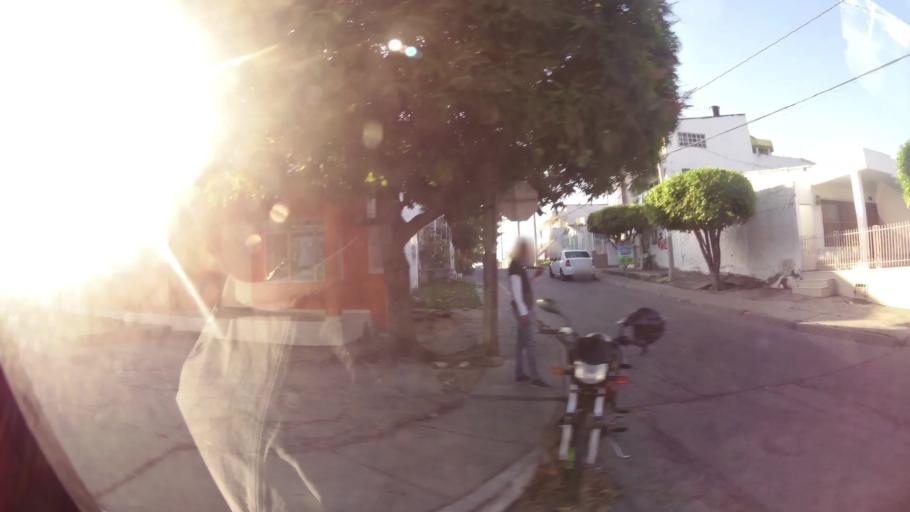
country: CO
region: Bolivar
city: Cartagena
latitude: 10.4033
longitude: -75.5184
